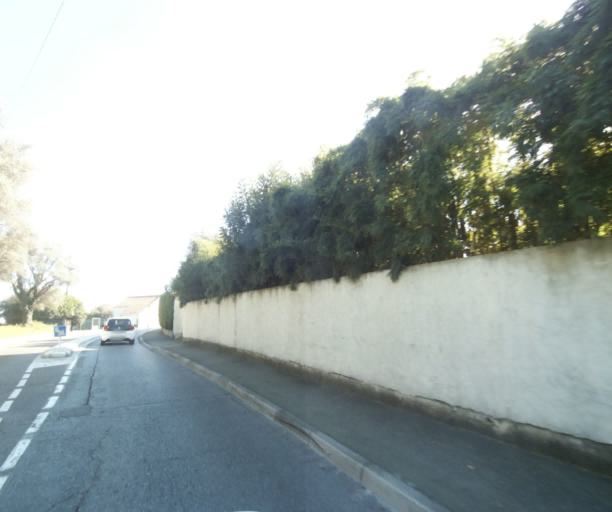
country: FR
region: Provence-Alpes-Cote d'Azur
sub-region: Departement des Alpes-Maritimes
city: Biot
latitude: 43.6028
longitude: 7.1062
